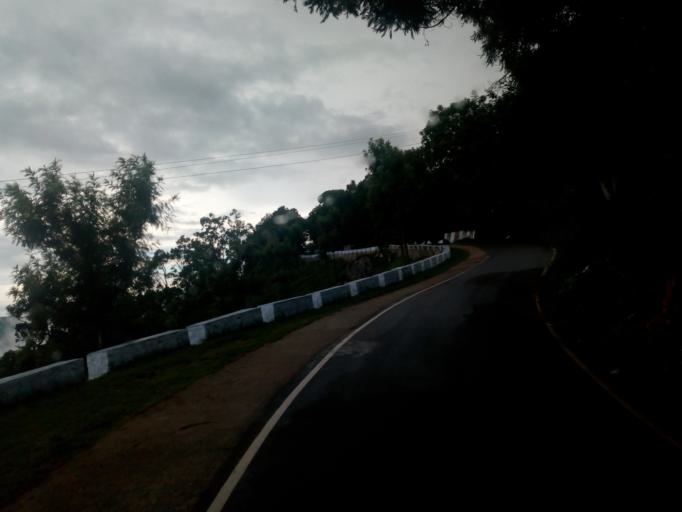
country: IN
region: Tamil Nadu
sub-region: Nilgiri
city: Kotagiri
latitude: 11.3628
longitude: 76.8483
